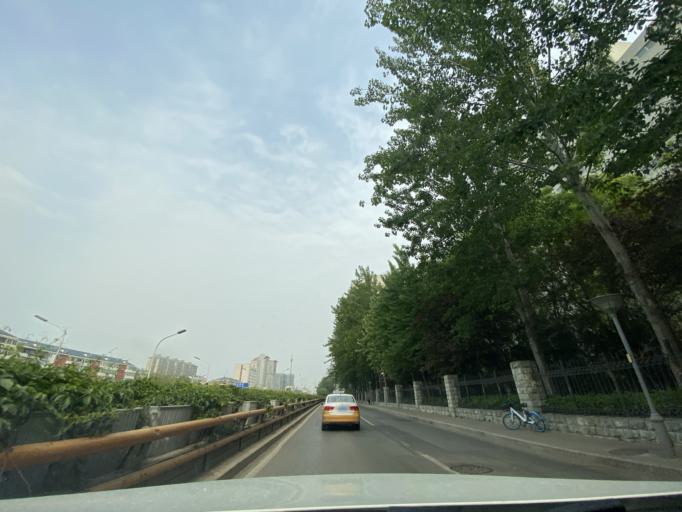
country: CN
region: Beijing
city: Qinghe
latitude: 39.9848
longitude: 116.3354
